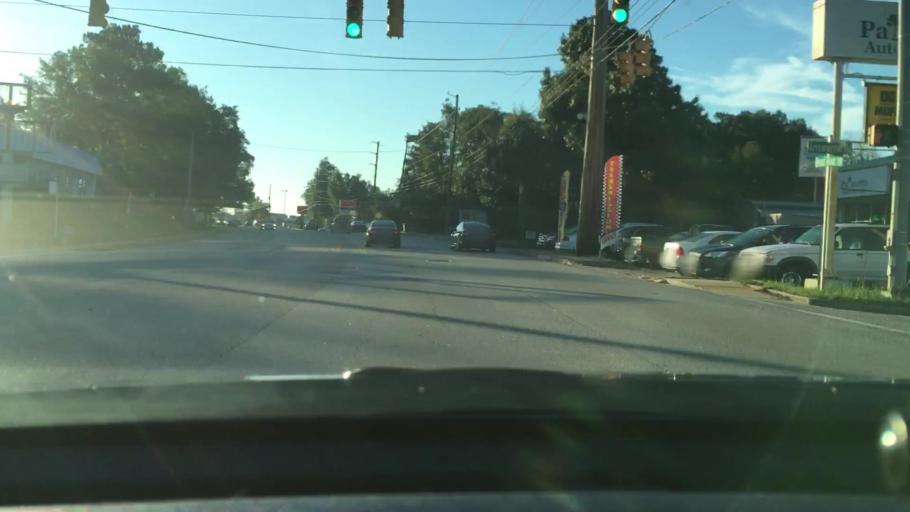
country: US
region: South Carolina
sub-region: Lexington County
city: West Columbia
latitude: 34.0272
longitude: -81.0836
